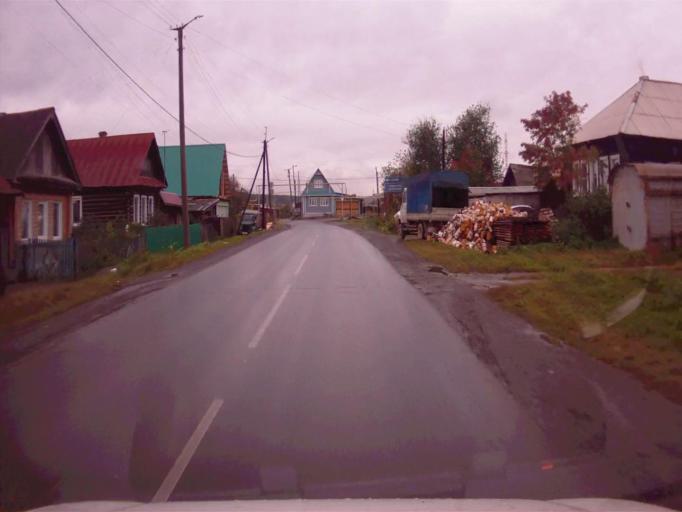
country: RU
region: Chelyabinsk
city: Verkhniy Ufaley
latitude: 56.0483
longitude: 60.2095
